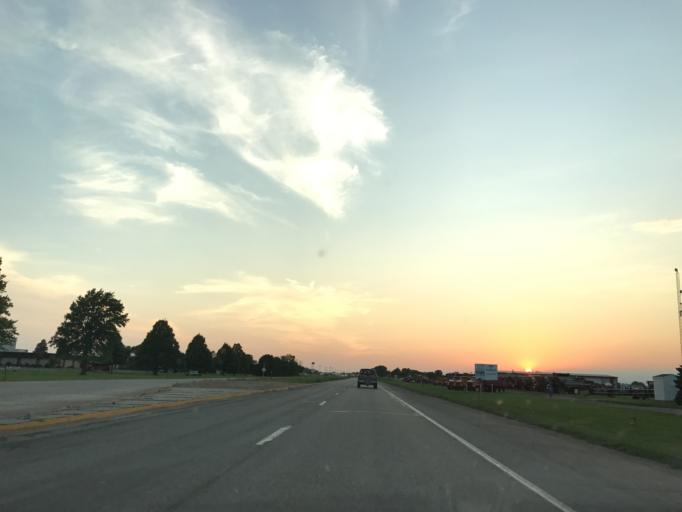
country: US
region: Nebraska
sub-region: Platte County
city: Columbus
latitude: 41.4386
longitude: -97.2916
